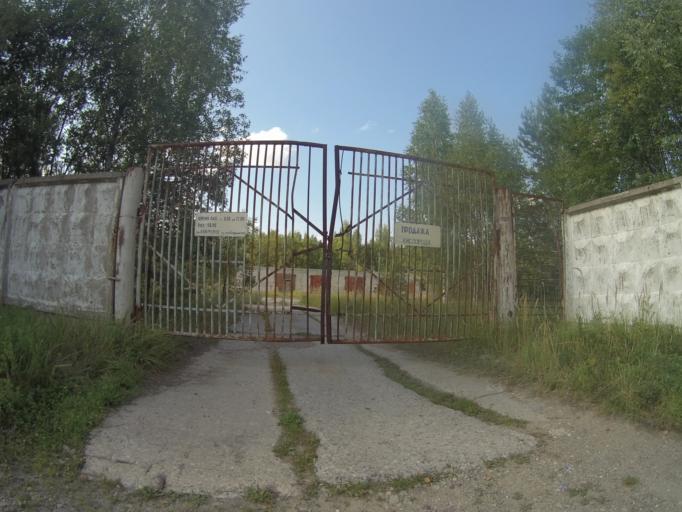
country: RU
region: Vladimir
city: Raduzhnyy
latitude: 55.9790
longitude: 40.2689
